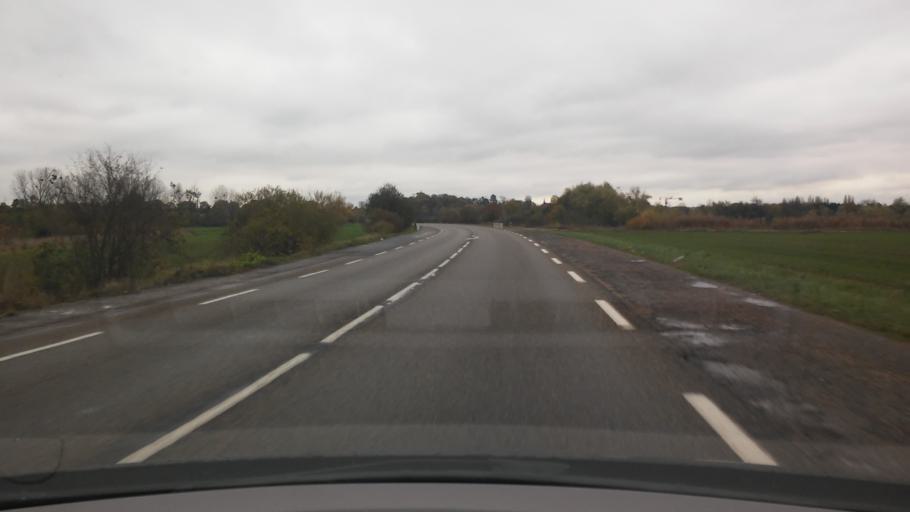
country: FR
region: Lorraine
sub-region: Departement de la Moselle
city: Ay-sur-Moselle
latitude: 49.2548
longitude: 6.1902
